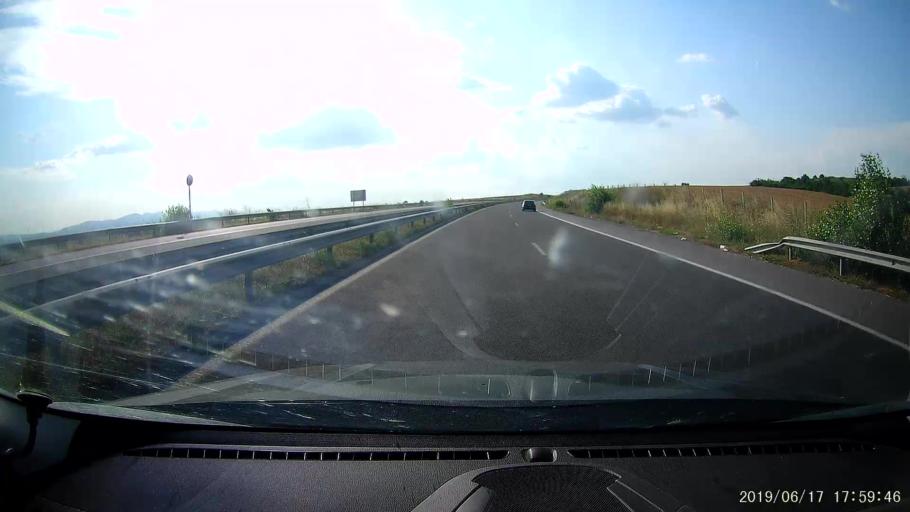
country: BG
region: Khaskovo
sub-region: Obshtina Svilengrad
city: Svilengrad
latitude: 41.7266
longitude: 26.2899
